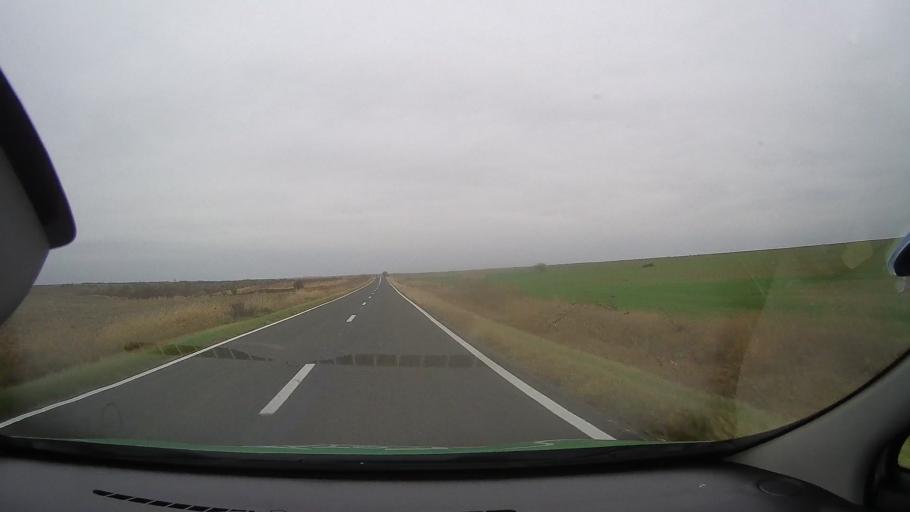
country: RO
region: Constanta
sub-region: Comuna Saraiu
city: Saraiu
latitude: 44.7109
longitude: 28.0992
